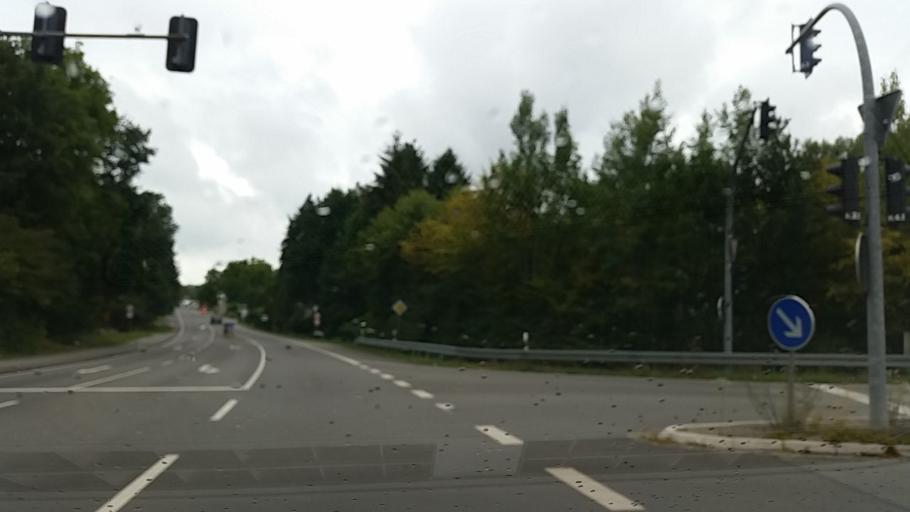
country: DE
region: Lower Saxony
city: Hasbergen
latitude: 52.2696
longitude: 7.9613
